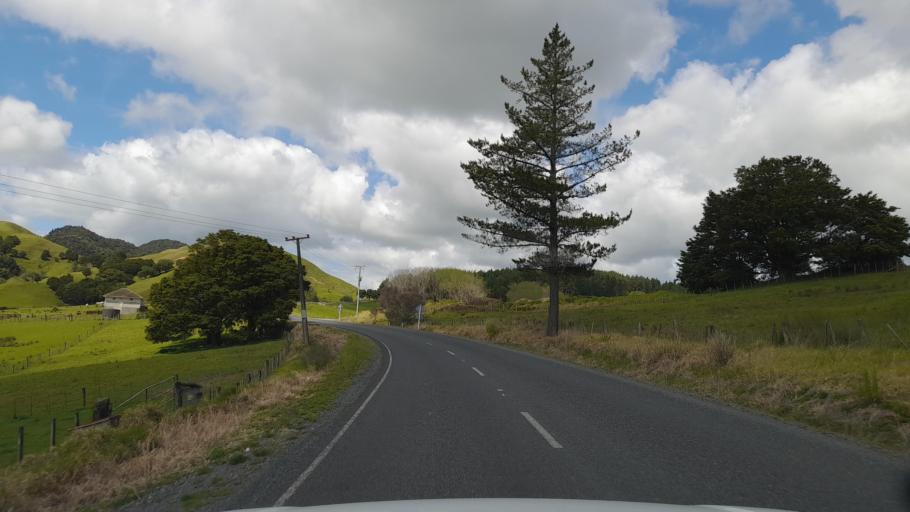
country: NZ
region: Northland
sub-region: Whangarei
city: Maungatapere
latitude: -35.6404
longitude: 174.1129
